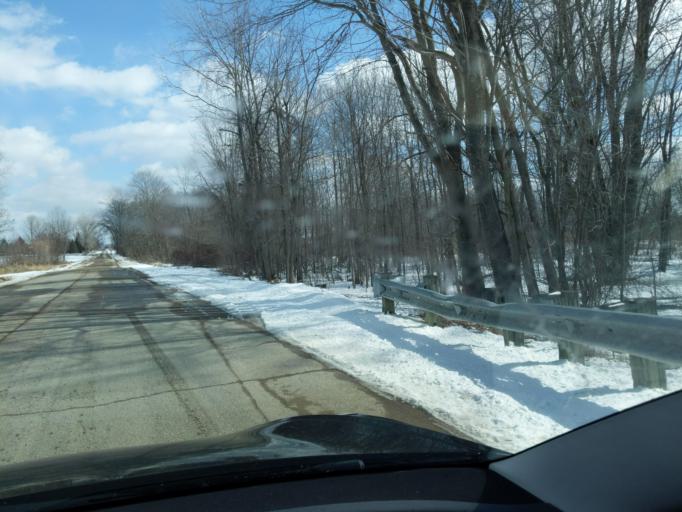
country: US
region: Michigan
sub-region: Livingston County
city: Fowlerville
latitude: 42.6139
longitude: -84.0806
